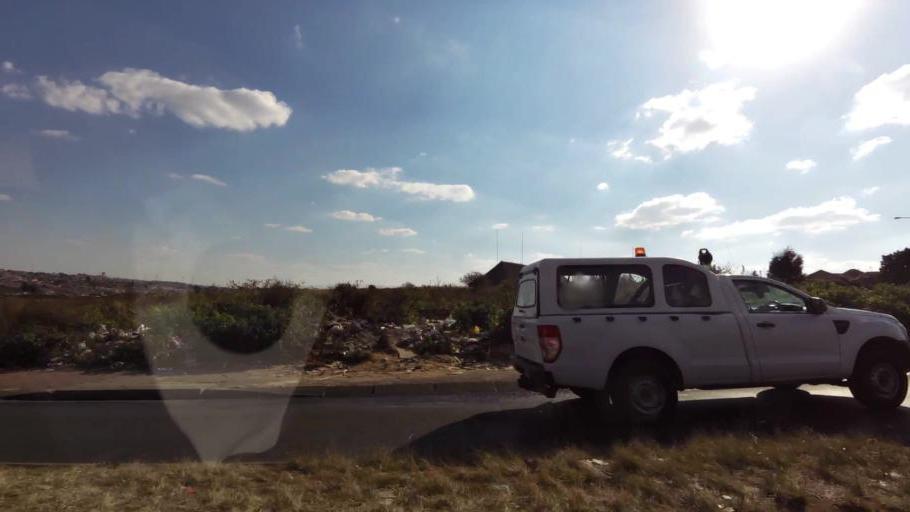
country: ZA
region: Gauteng
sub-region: City of Johannesburg Metropolitan Municipality
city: Soweto
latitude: -26.2221
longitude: 27.8888
